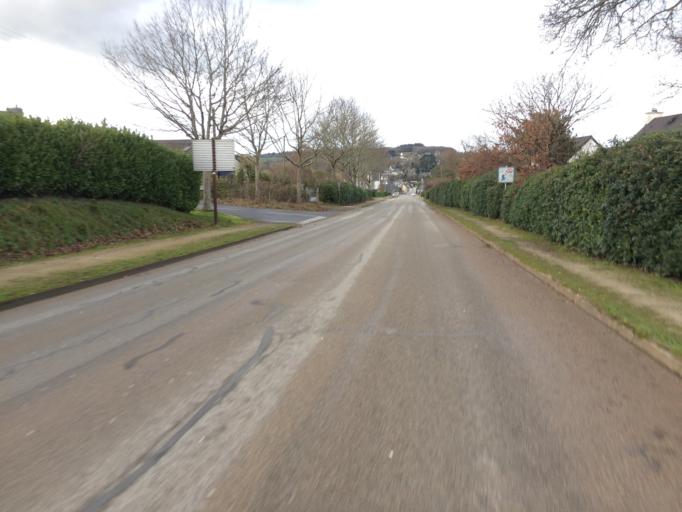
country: FR
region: Brittany
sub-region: Departement du Finistere
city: Daoulas
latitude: 48.3543
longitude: -4.2560
